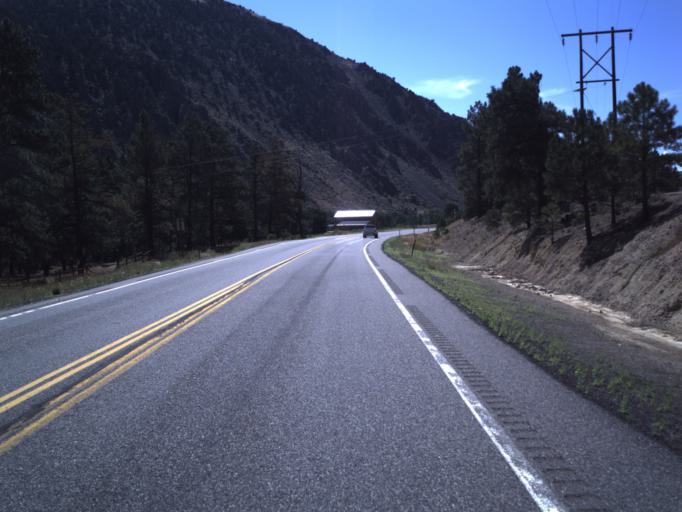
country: US
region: Utah
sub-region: Sevier County
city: Monroe
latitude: 38.5130
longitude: -112.2631
